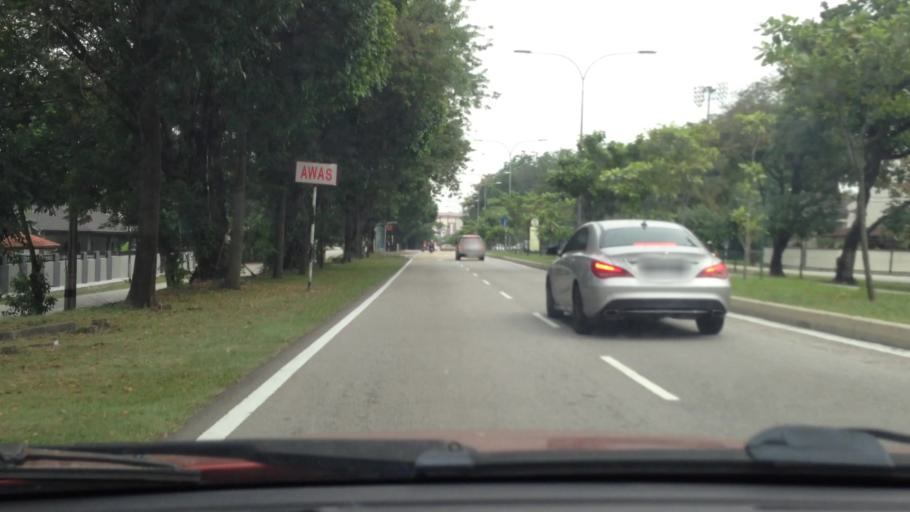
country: MY
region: Selangor
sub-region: Petaling
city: Petaling Jaya
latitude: 3.0970
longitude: 101.6072
